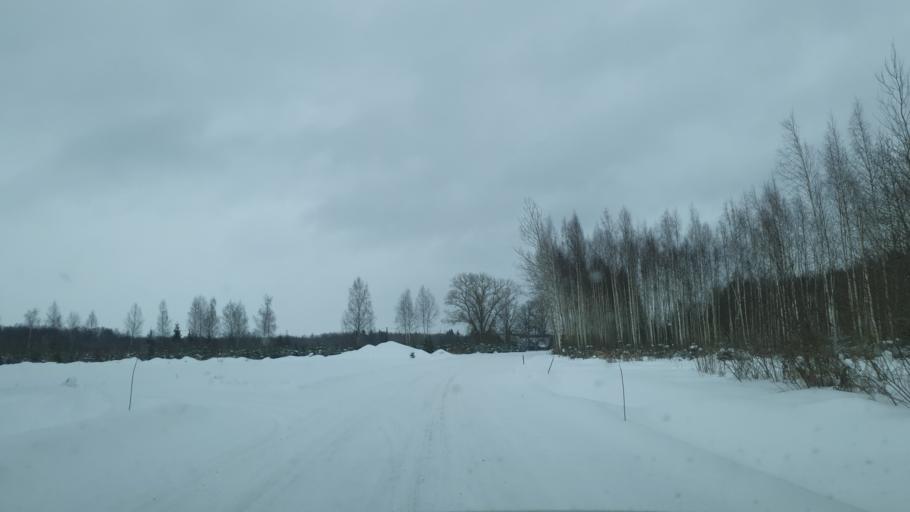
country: EE
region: Polvamaa
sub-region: Raepina vald
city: Rapina
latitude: 58.2079
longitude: 27.3065
